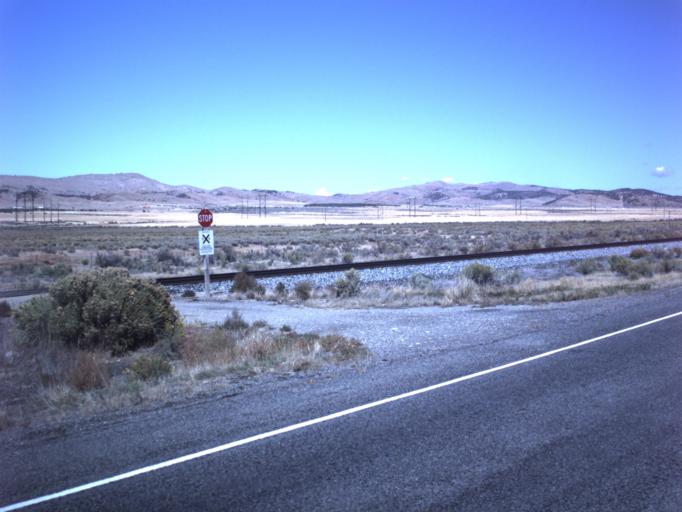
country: US
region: Utah
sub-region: Juab County
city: Nephi
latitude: 39.5385
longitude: -111.9291
